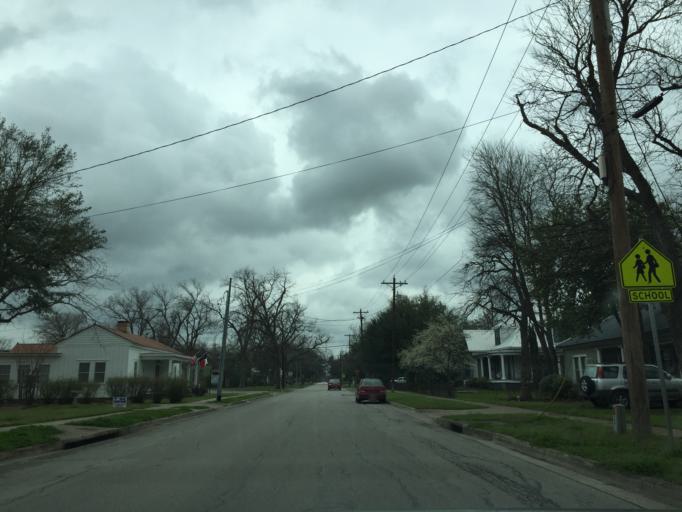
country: US
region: Texas
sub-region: Bastrop County
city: Bastrop
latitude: 30.1118
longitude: -97.3175
